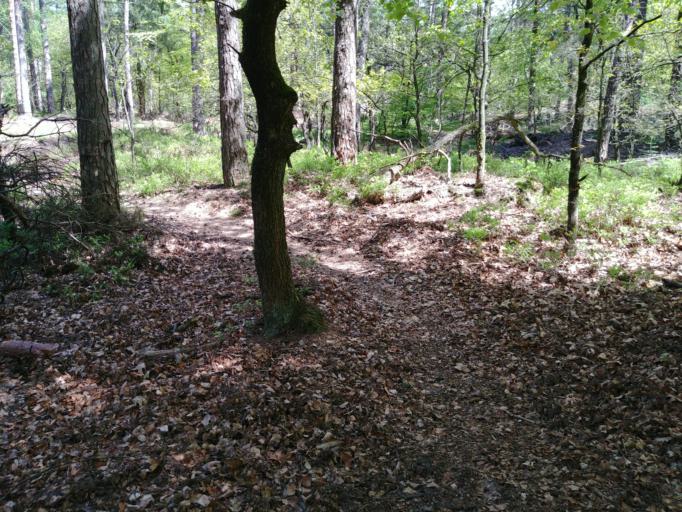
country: NL
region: Gelderland
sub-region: Gemeente Barneveld
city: Garderen
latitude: 52.3059
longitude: 5.7086
